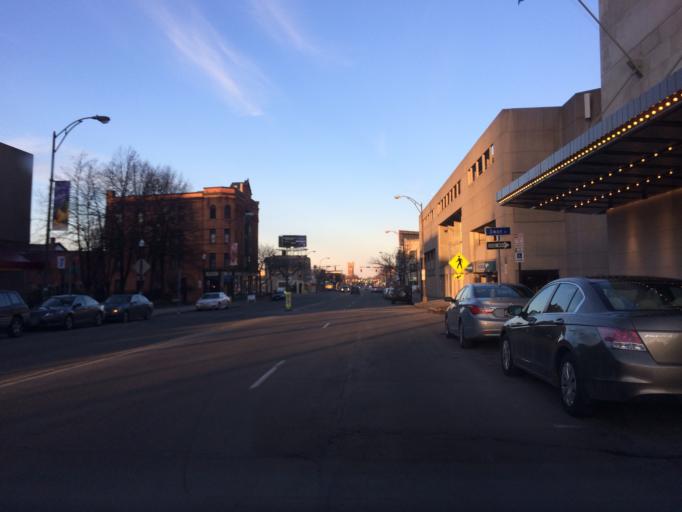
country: US
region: New York
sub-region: Monroe County
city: Rochester
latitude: 43.1583
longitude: -77.6007
